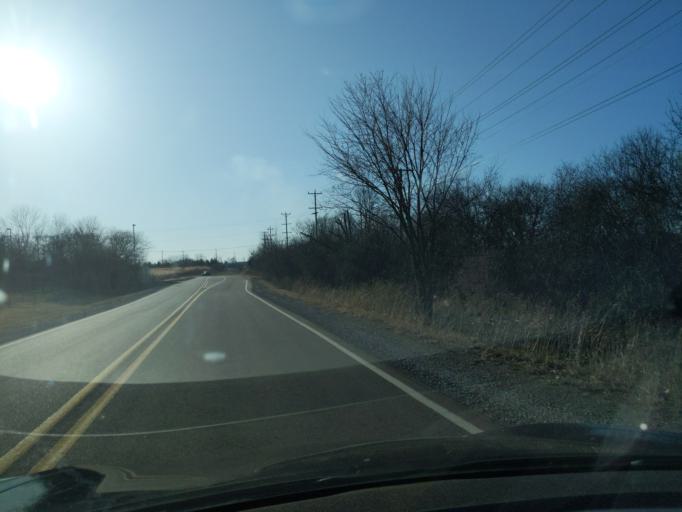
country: US
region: Michigan
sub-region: Washtenaw County
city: Ann Arbor
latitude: 42.2432
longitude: -83.7630
